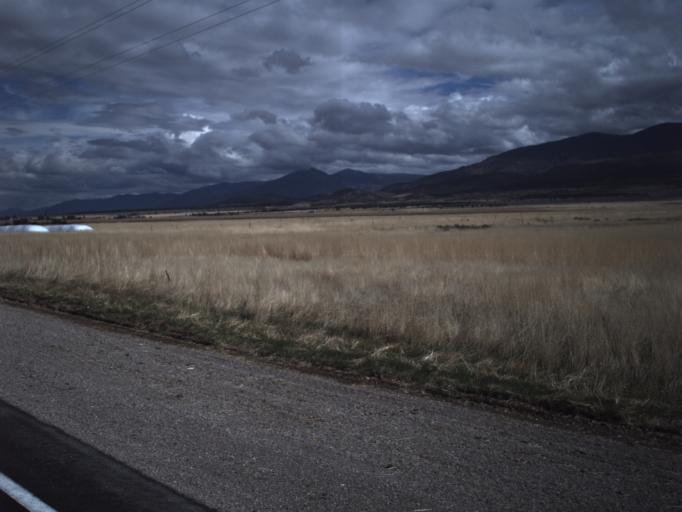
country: US
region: Utah
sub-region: Millard County
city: Fillmore
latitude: 38.8542
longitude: -112.4212
